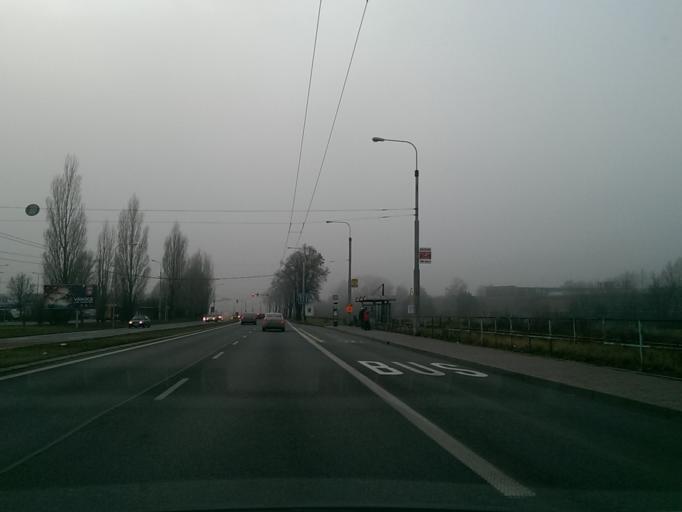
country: CZ
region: Zlin
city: Tecovice
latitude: 49.2053
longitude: 17.5716
